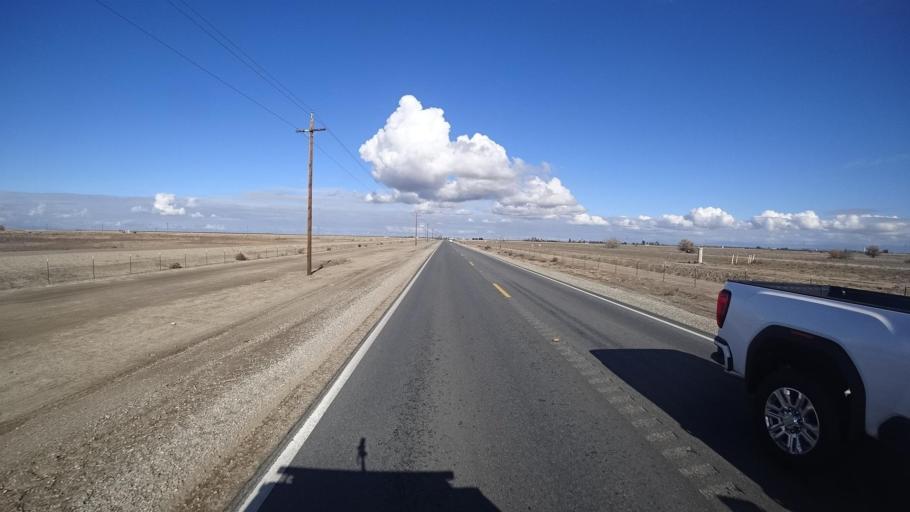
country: US
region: California
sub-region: Kern County
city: Rosedale
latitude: 35.3412
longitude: -119.2523
